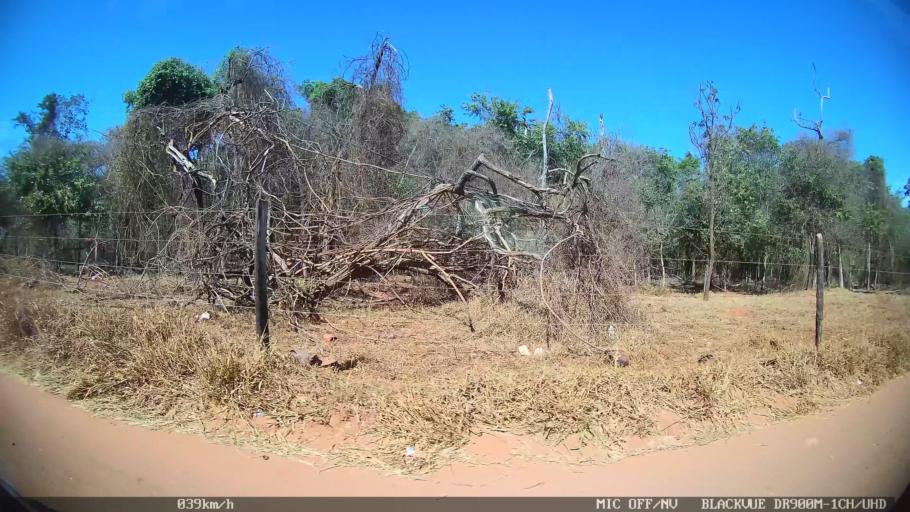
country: BR
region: Sao Paulo
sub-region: Sao Jose Do Rio Preto
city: Sao Jose do Rio Preto
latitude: -20.7423
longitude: -49.4289
